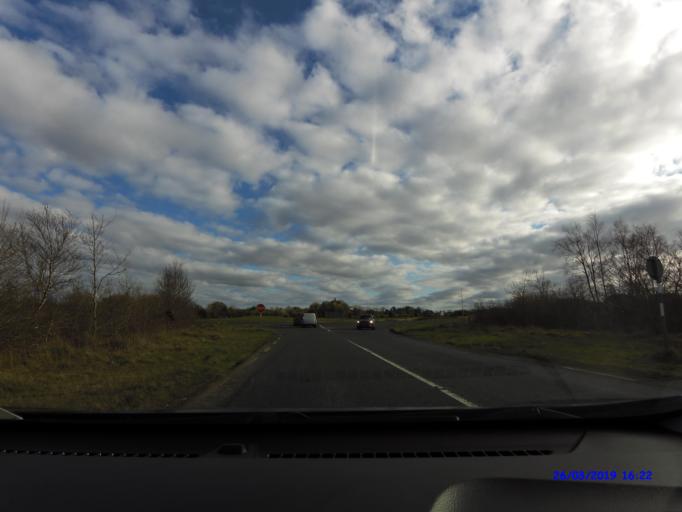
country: IE
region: Connaught
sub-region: Maigh Eo
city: Swinford
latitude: 53.9277
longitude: -8.9599
